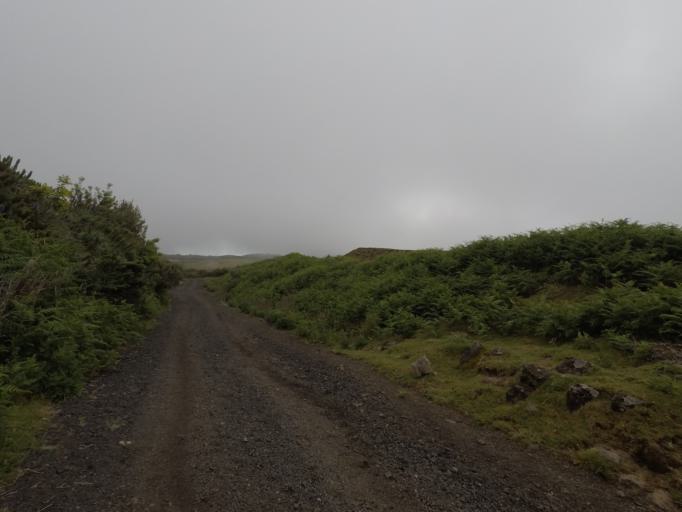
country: PT
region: Madeira
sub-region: Funchal
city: Nossa Senhora do Monte
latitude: 32.7252
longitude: -16.8866
